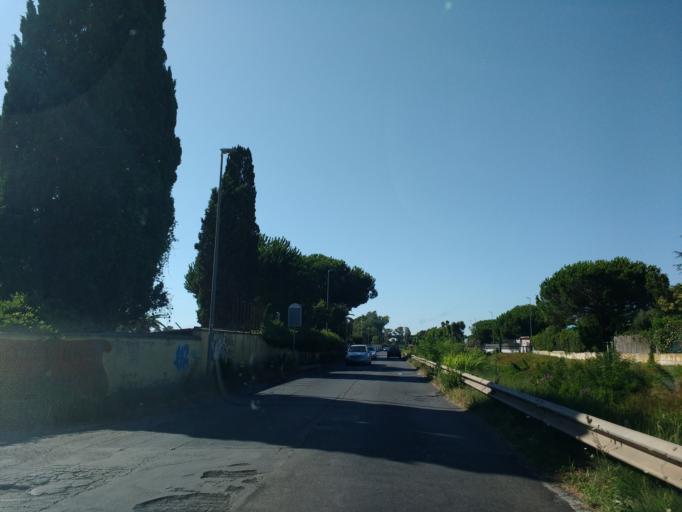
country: IT
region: Latium
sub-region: Citta metropolitana di Roma Capitale
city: Acilia-Castel Fusano-Ostia Antica
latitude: 41.7468
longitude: 12.3340
